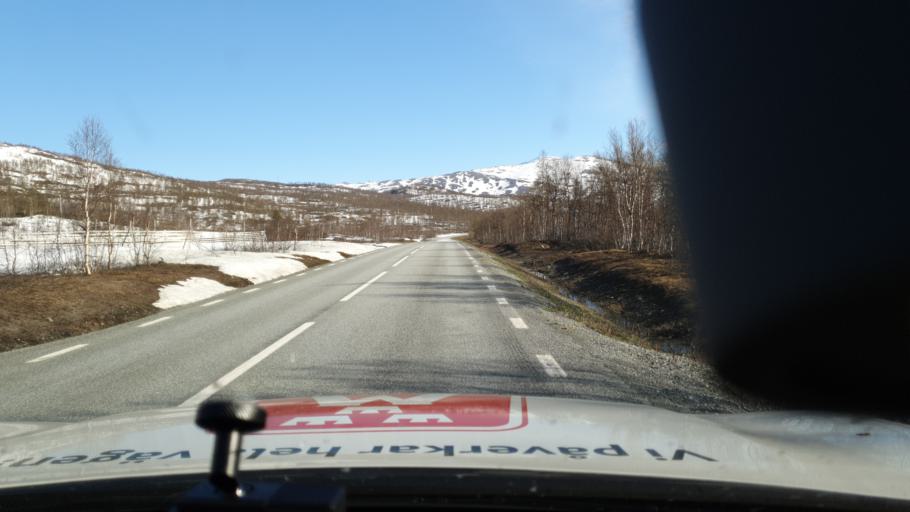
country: NO
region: Nordland
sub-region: Rana
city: Mo i Rana
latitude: 66.0759
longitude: 14.8709
